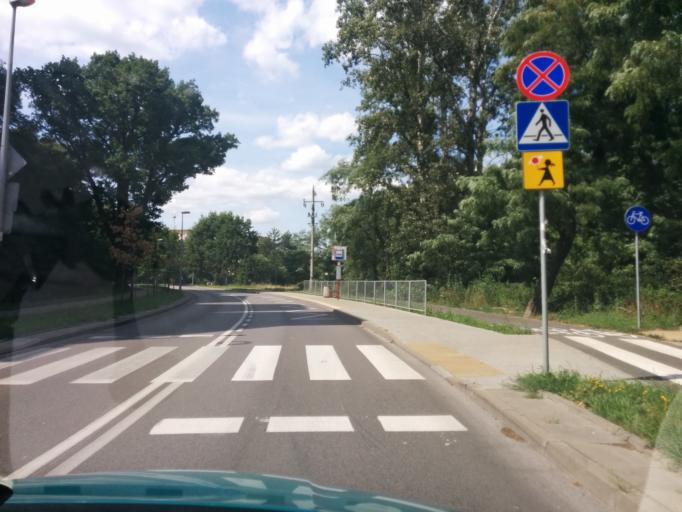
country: PL
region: Masovian Voivodeship
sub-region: Warszawa
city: Bialoleka
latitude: 52.3228
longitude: 20.9649
